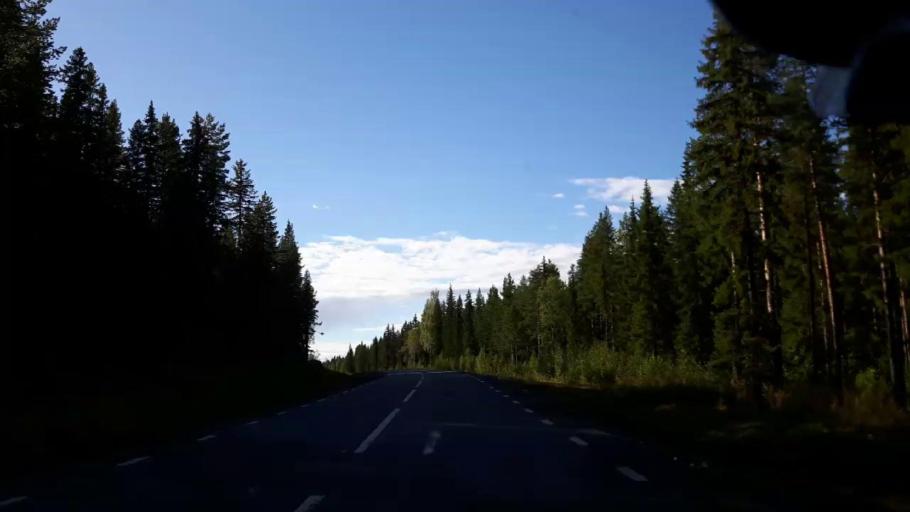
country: SE
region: Jaemtland
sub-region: Ragunda Kommun
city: Hammarstrand
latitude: 63.5359
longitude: 16.0372
